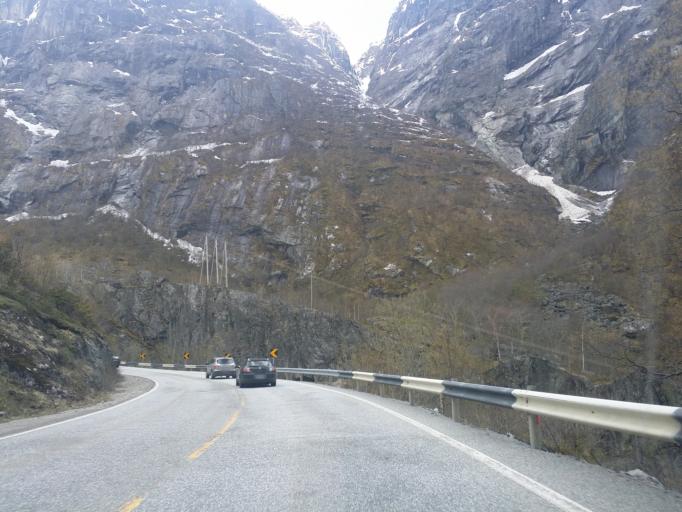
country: NO
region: Hordaland
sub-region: Eidfjord
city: Eidfjord
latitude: 60.4177
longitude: 7.1926
